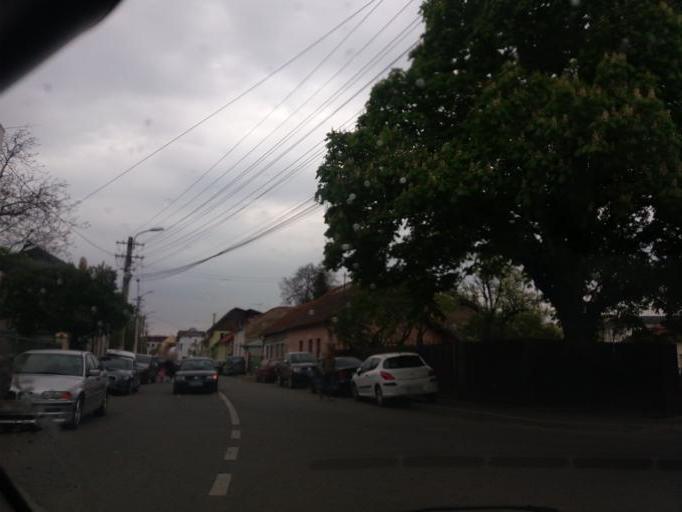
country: RO
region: Cluj
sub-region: Municipiul Cluj-Napoca
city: Cluj-Napoca
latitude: 46.7651
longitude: 23.5703
